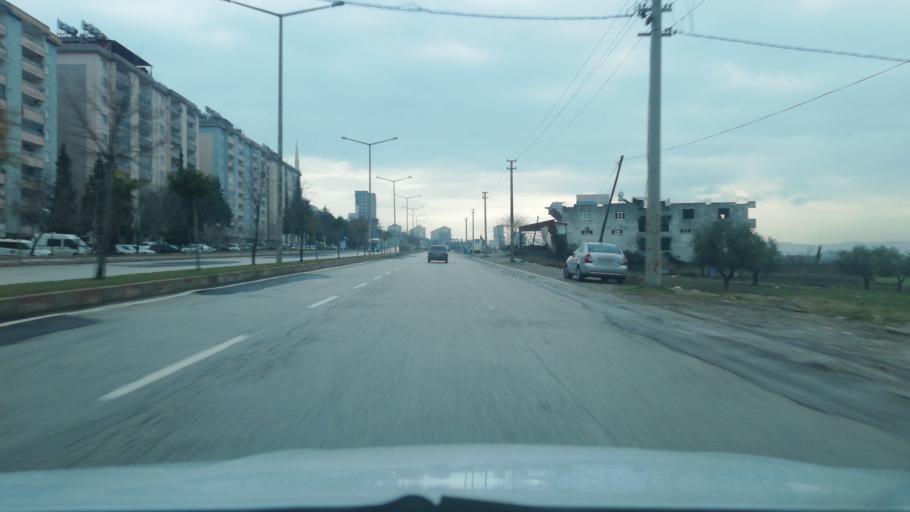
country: TR
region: Kahramanmaras
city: Kahramanmaras
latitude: 37.5829
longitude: 36.9831
